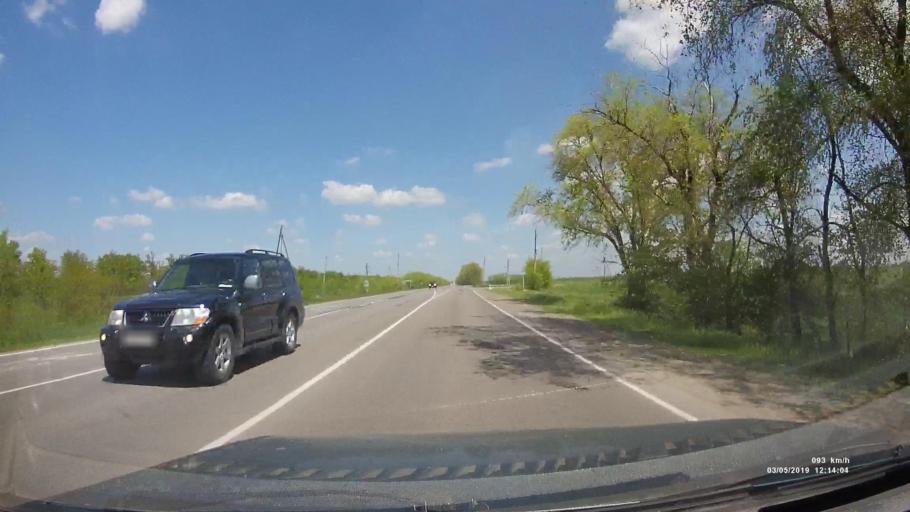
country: RU
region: Rostov
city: Melikhovskaya
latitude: 47.3391
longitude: 40.5598
